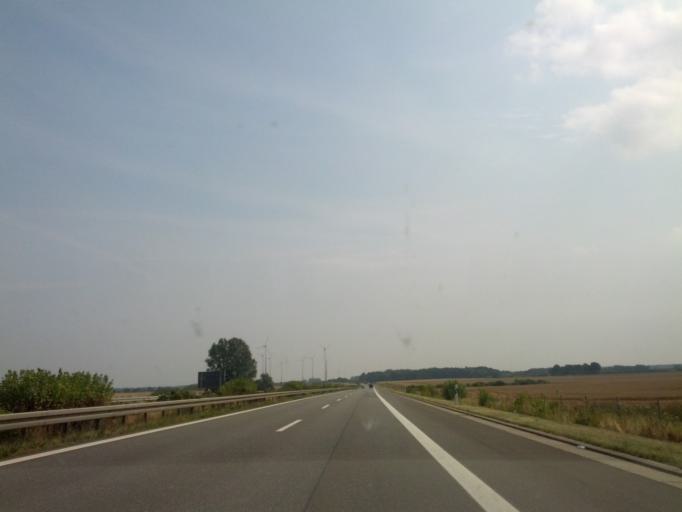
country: DE
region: Mecklenburg-Vorpommern
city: Grimmen
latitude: 54.0853
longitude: 12.9952
